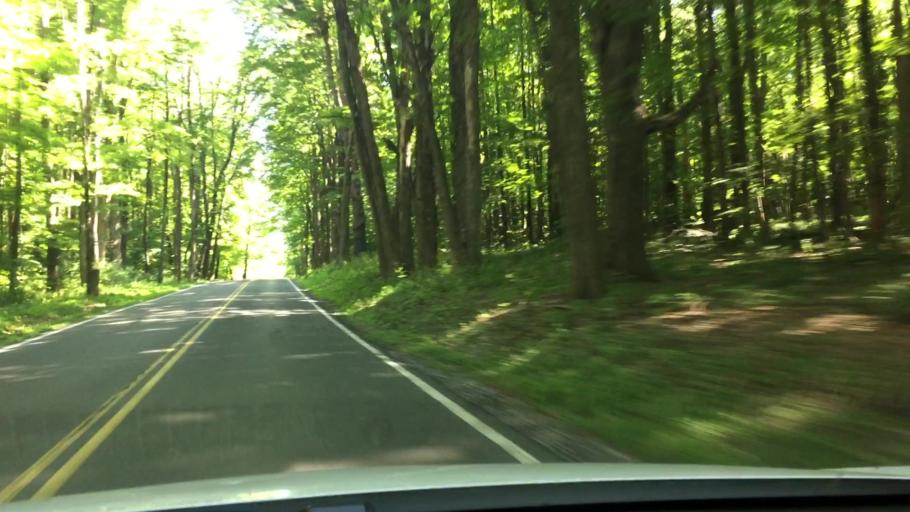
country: US
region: Massachusetts
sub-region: Berkshire County
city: Richmond
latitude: 42.3920
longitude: -73.3374
